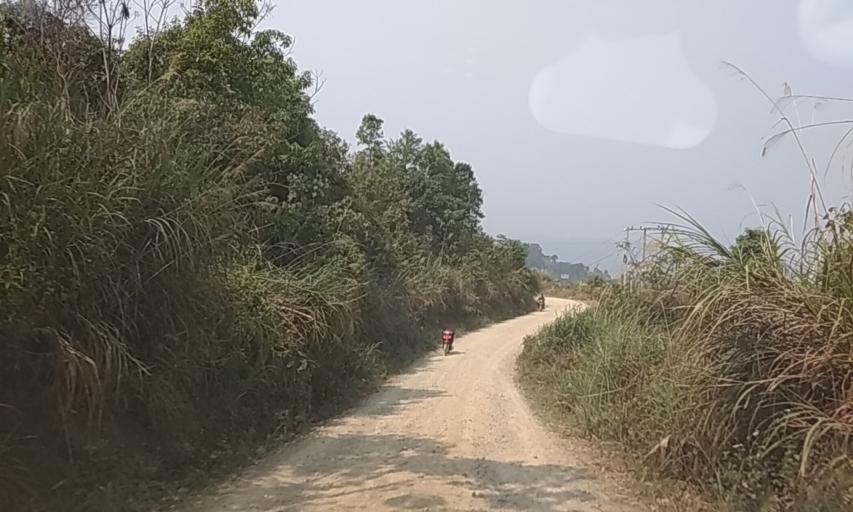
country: TH
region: Nan
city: Chaloem Phra Kiat
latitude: 20.0517
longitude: 101.0735
